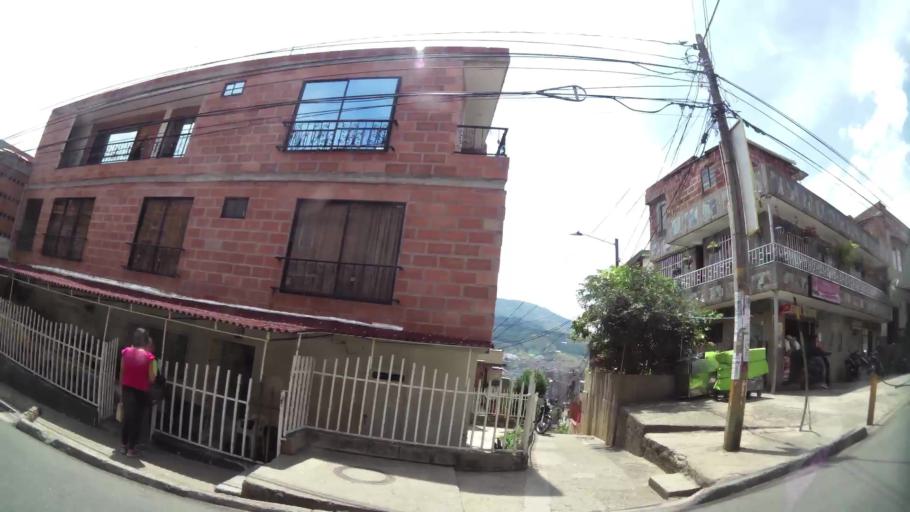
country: CO
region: Antioquia
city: Bello
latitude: 6.3459
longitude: -75.5477
